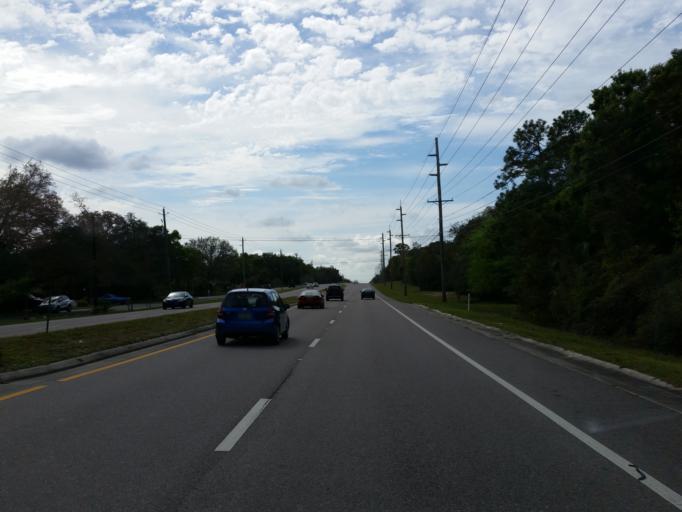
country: US
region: Florida
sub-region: Hillsborough County
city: Temple Terrace
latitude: 28.0693
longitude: -82.3851
